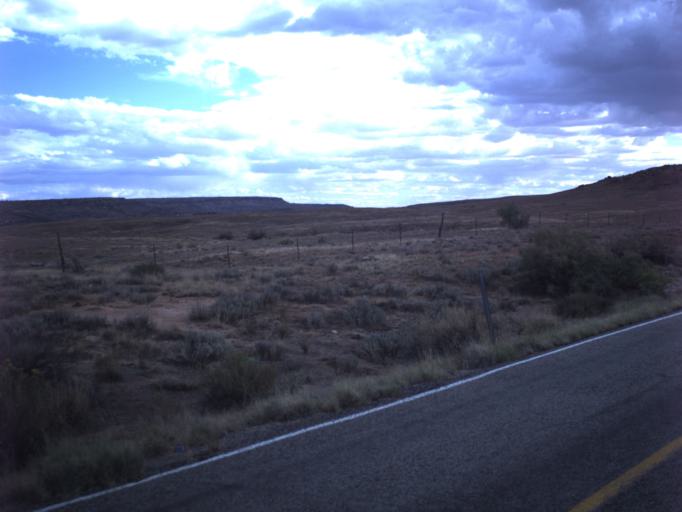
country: US
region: Utah
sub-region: San Juan County
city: Blanding
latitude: 37.4221
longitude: -109.4193
